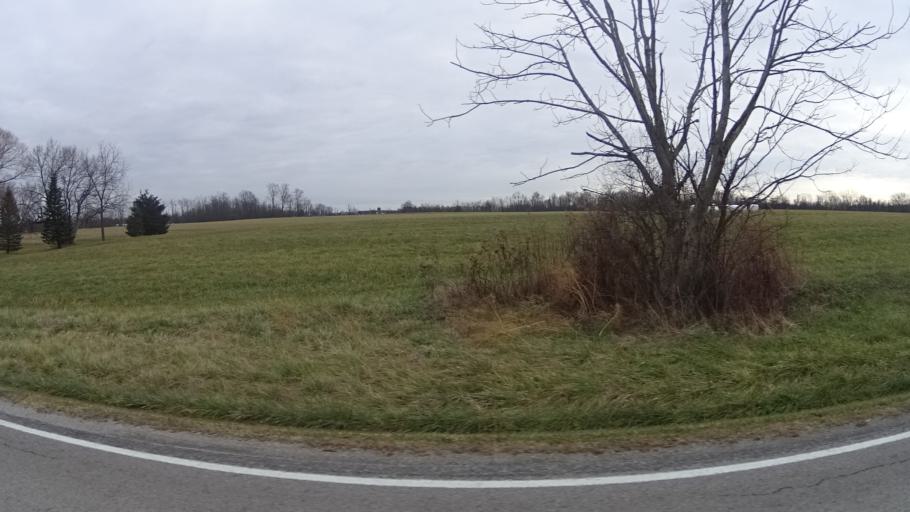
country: US
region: Ohio
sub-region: Lorain County
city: Wellington
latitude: 41.1459
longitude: -82.2692
